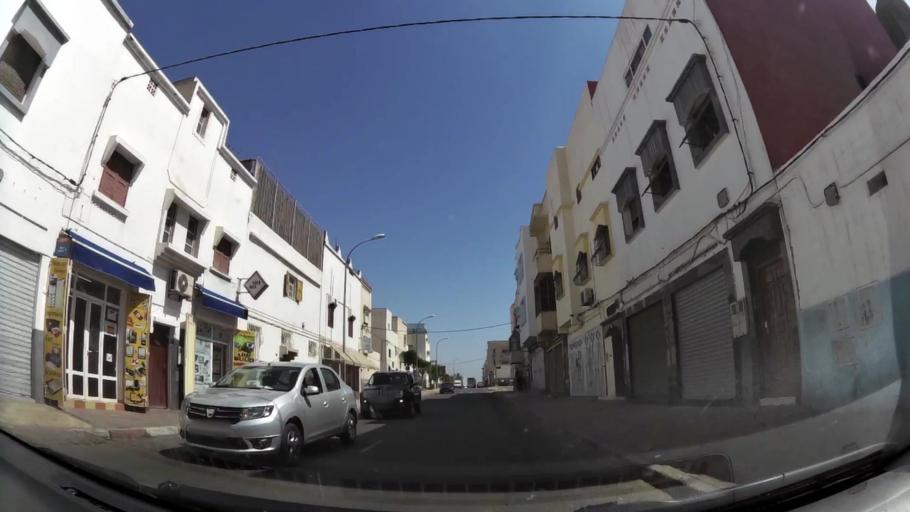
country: MA
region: Souss-Massa-Draa
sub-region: Agadir-Ida-ou-Tnan
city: Agadir
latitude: 30.4139
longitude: -9.5849
